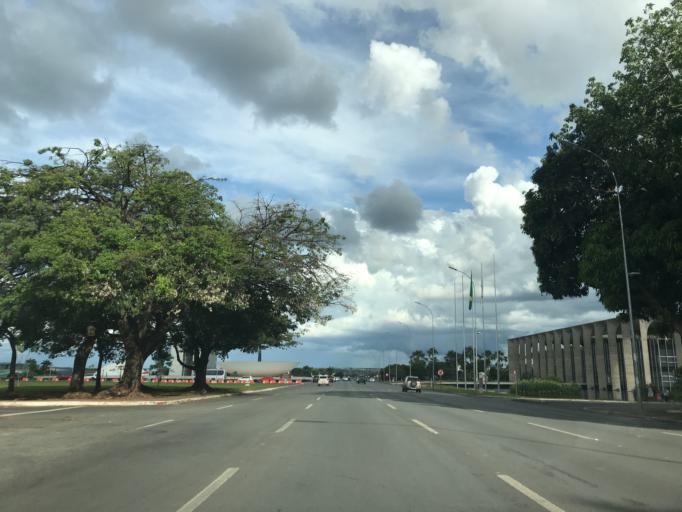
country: BR
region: Federal District
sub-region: Brasilia
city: Brasilia
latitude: -15.7994
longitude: -47.8685
